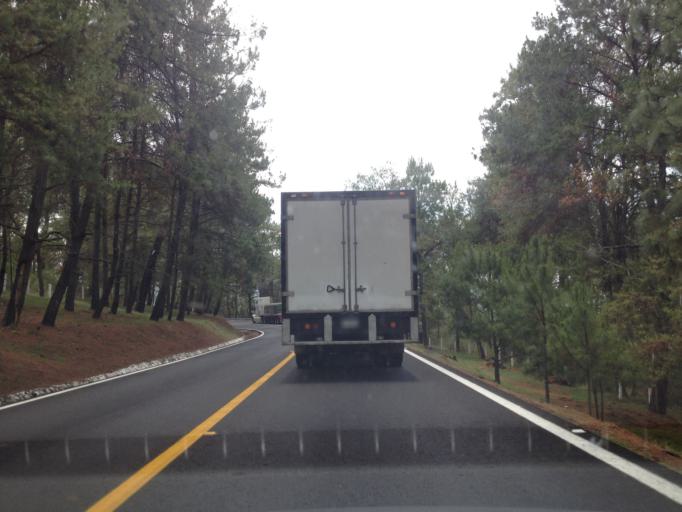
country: MX
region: Michoacan
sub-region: Patzcuaro
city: Santa Maria Huiramangaro (San Juan Tumbio)
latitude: 19.4987
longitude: -101.7527
